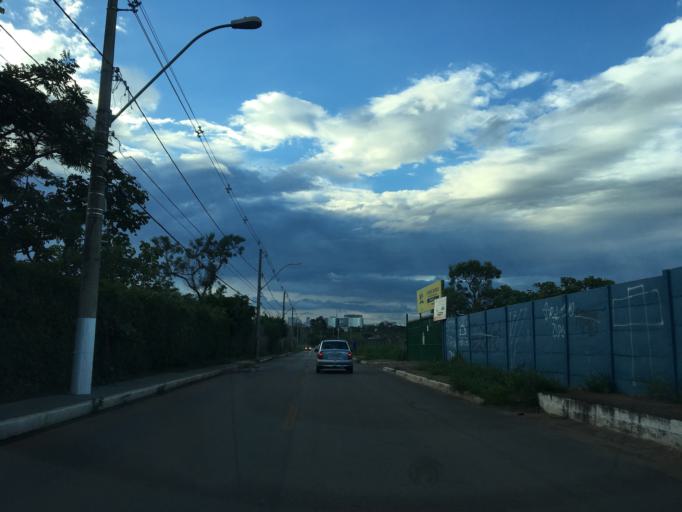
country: BR
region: Federal District
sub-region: Brasilia
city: Brasilia
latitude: -15.8153
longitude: -47.8453
